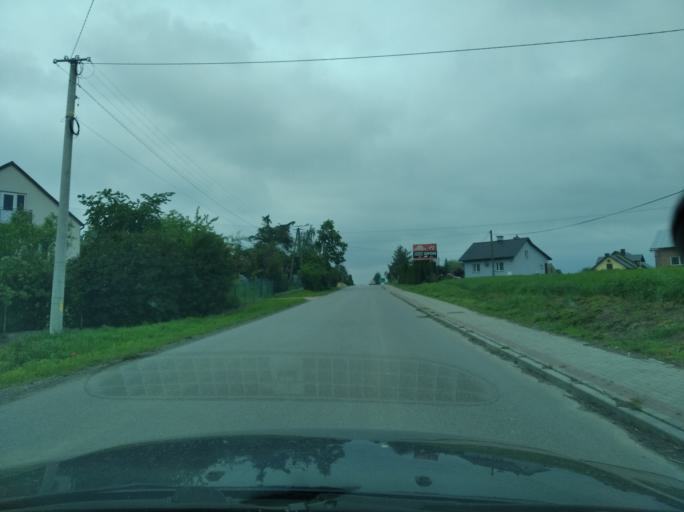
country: PL
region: Subcarpathian Voivodeship
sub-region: Powiat ropczycko-sedziszowski
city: Sedziszow Malopolski
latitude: 50.0866
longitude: 21.6658
